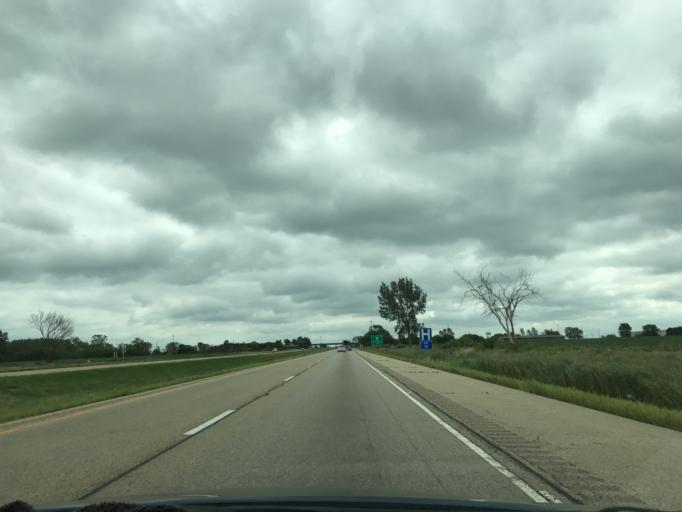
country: US
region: Illinois
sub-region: Bureau County
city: Ladd
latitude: 41.3693
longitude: -89.2291
